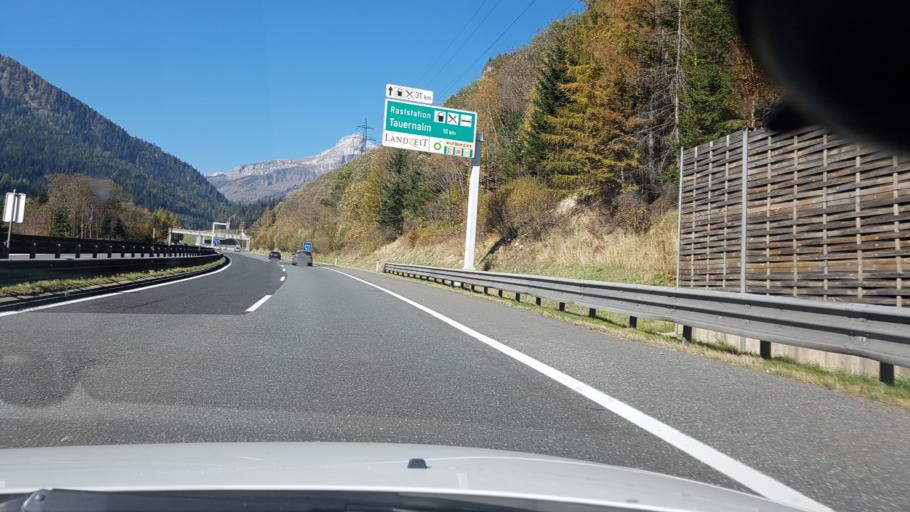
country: AT
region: Salzburg
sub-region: Politischer Bezirk Tamsweg
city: Zederhaus
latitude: 47.1692
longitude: 13.4634
